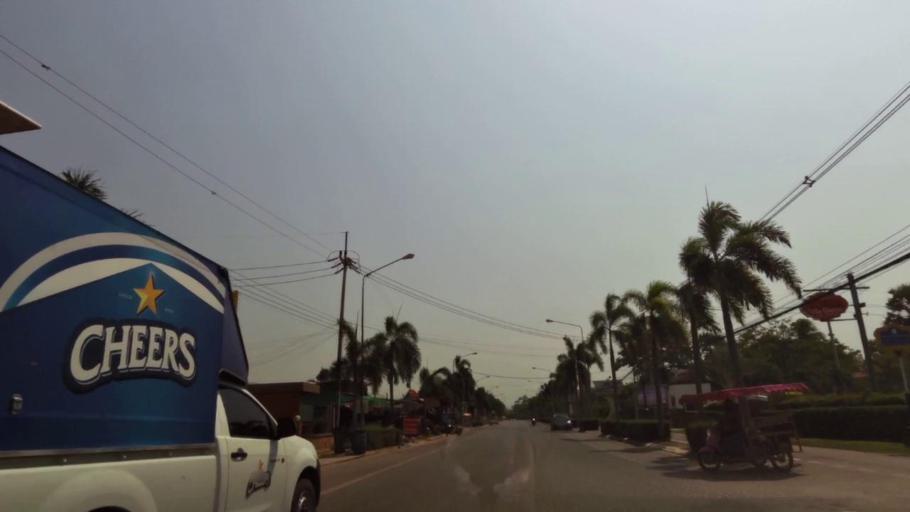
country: TH
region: Chanthaburi
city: Tha Mai
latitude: 12.5540
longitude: 101.9212
